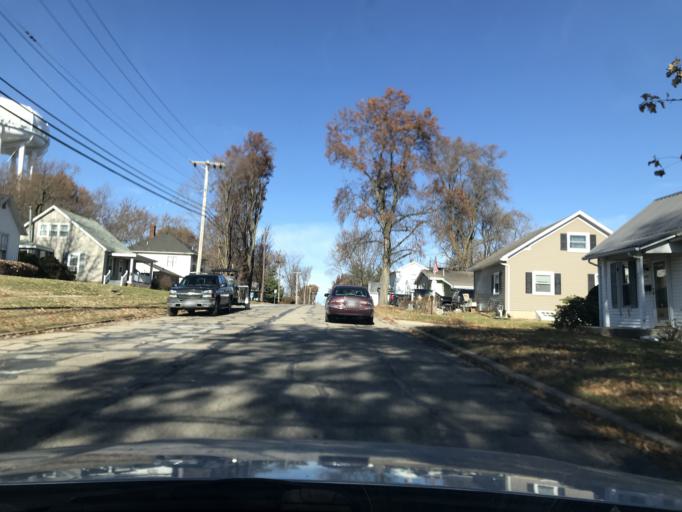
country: US
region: Illinois
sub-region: McDonough County
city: Macomb
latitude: 40.4523
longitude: -90.6673
